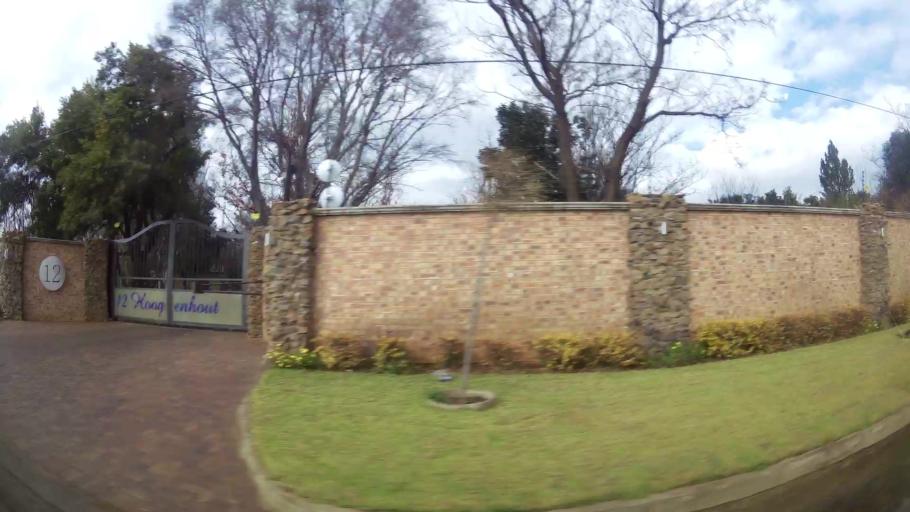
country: ZA
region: Gauteng
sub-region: Sedibeng District Municipality
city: Meyerton
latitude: -26.5878
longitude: 28.0112
